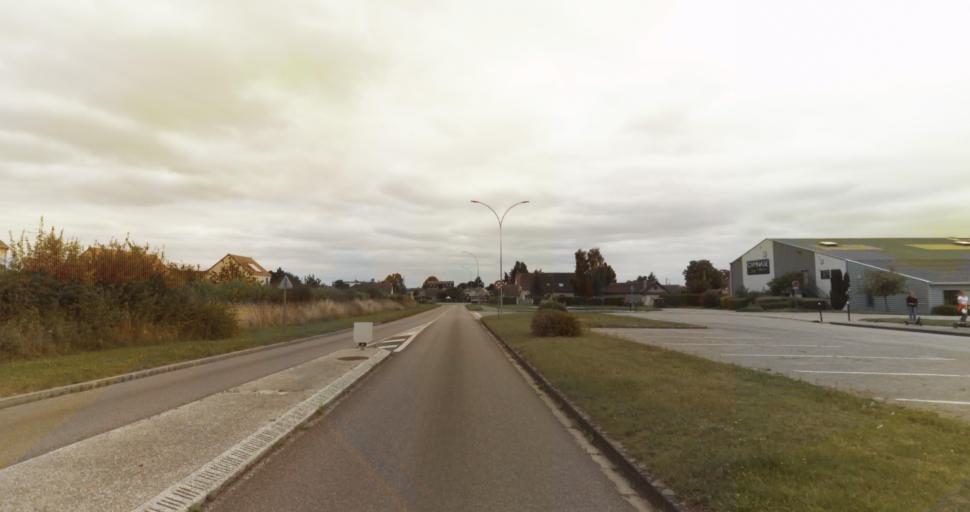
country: FR
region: Haute-Normandie
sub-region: Departement de l'Eure
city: Marcilly-sur-Eure
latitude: 48.9084
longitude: 1.2834
